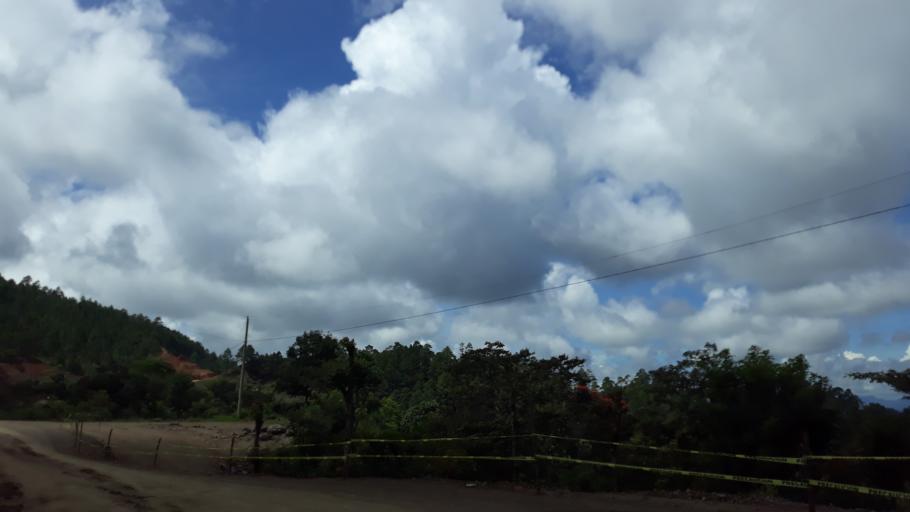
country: HN
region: El Paraiso
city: Santa Cruz
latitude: 13.7664
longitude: -86.6460
